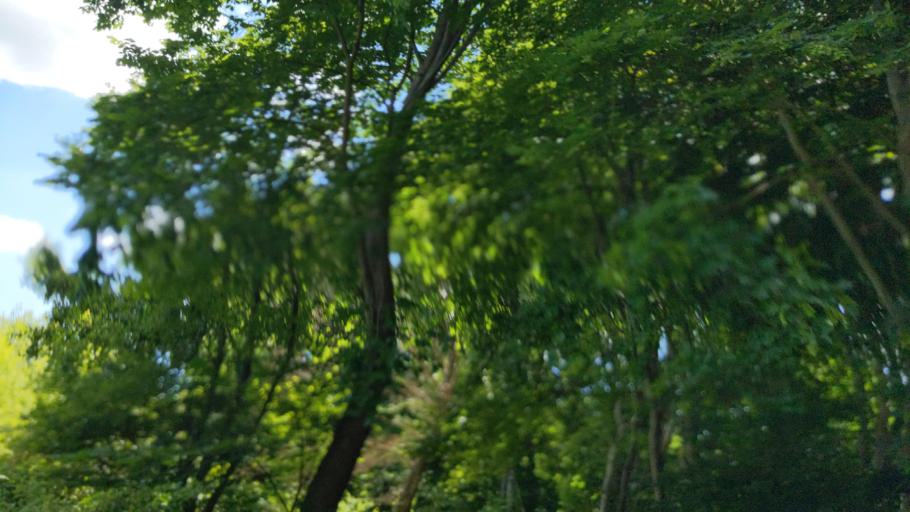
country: DE
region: Schleswig-Holstein
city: Buchholz
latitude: 53.7272
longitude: 10.7444
